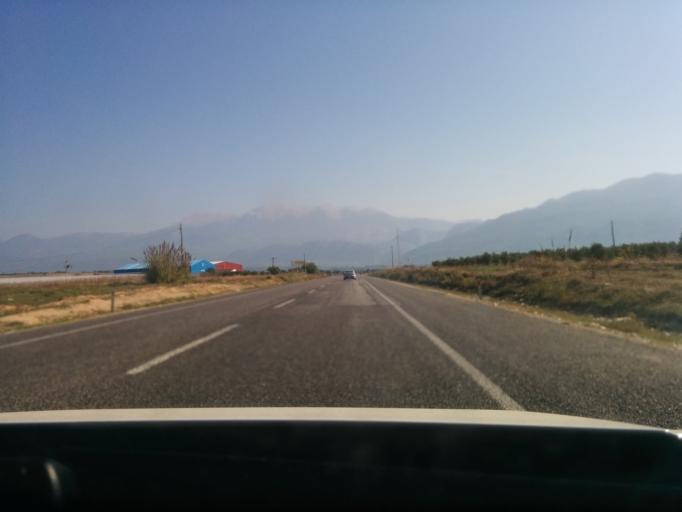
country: TR
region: Mugla
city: Esen
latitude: 36.4424
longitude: 29.2809
